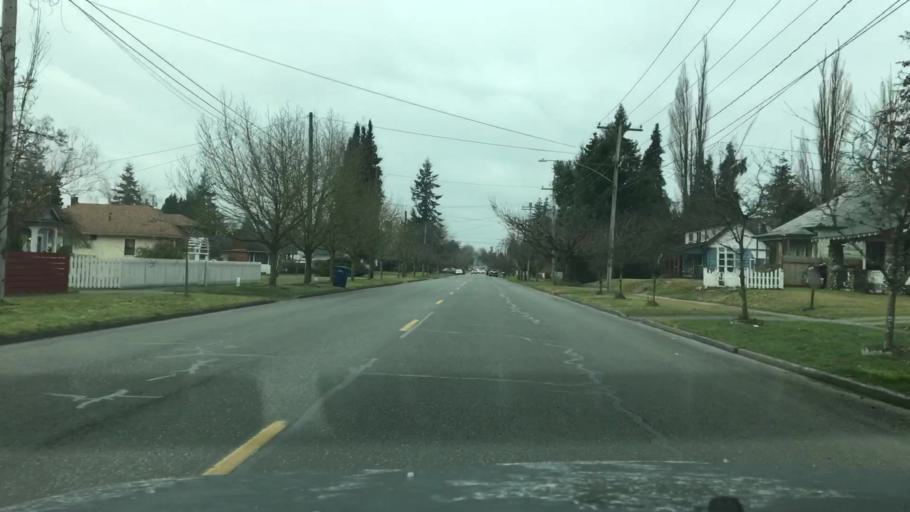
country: US
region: Washington
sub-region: Skagit County
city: Sedro-Woolley
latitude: 48.5053
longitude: -122.2266
